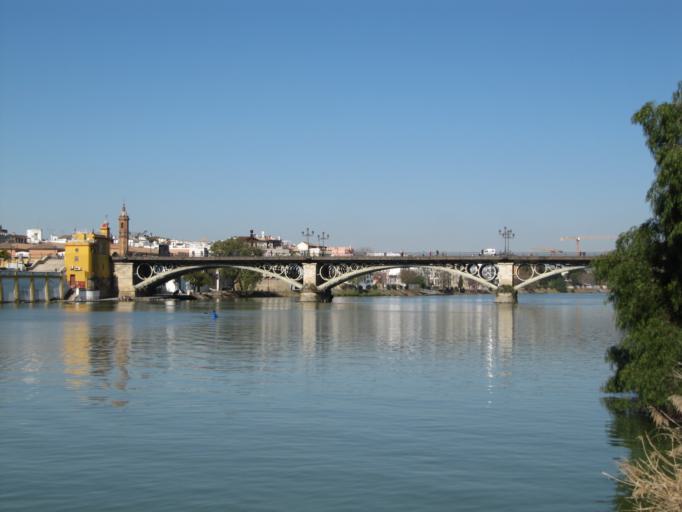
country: ES
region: Andalusia
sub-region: Provincia de Sevilla
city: Sevilla
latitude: 37.3865
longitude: -6.0009
